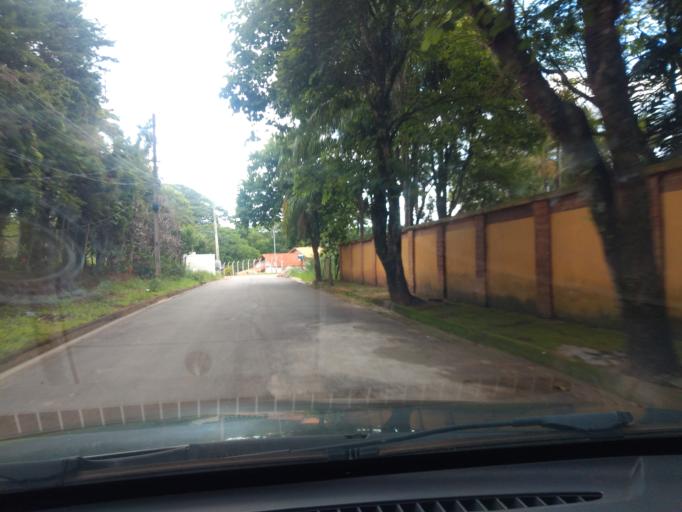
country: BR
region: Minas Gerais
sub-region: Tres Coracoes
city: Tres Coracoes
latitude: -21.6875
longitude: -45.2677
